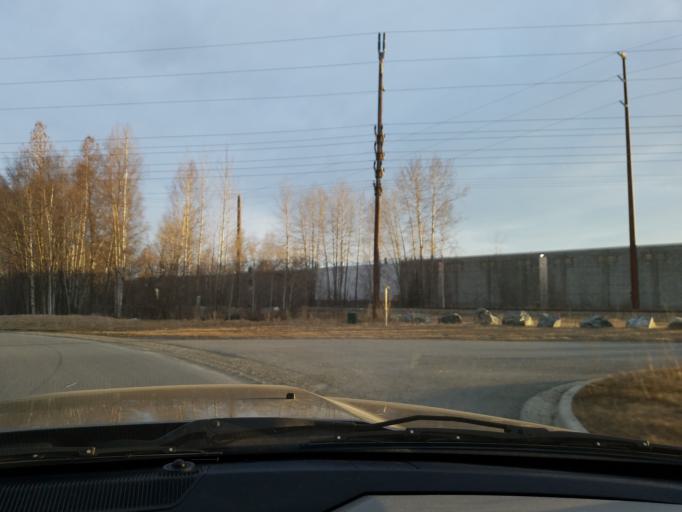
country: US
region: Alaska
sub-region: Anchorage Municipality
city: Anchorage
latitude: 61.1661
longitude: -149.8998
